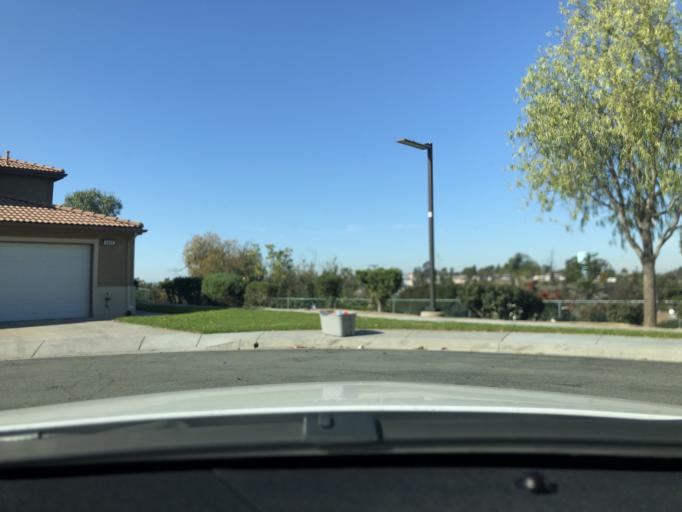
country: US
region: California
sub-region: San Diego County
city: Lemon Grove
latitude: 32.7413
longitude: -117.0634
